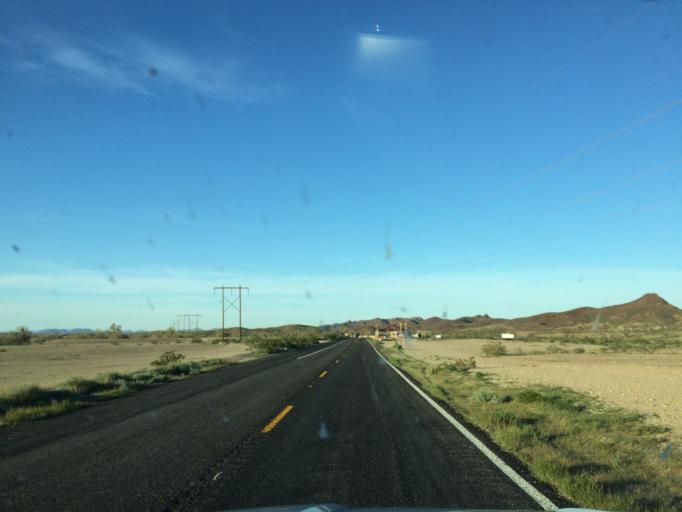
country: MX
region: Baja California
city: Los Algodones
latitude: 33.1331
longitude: -114.8805
